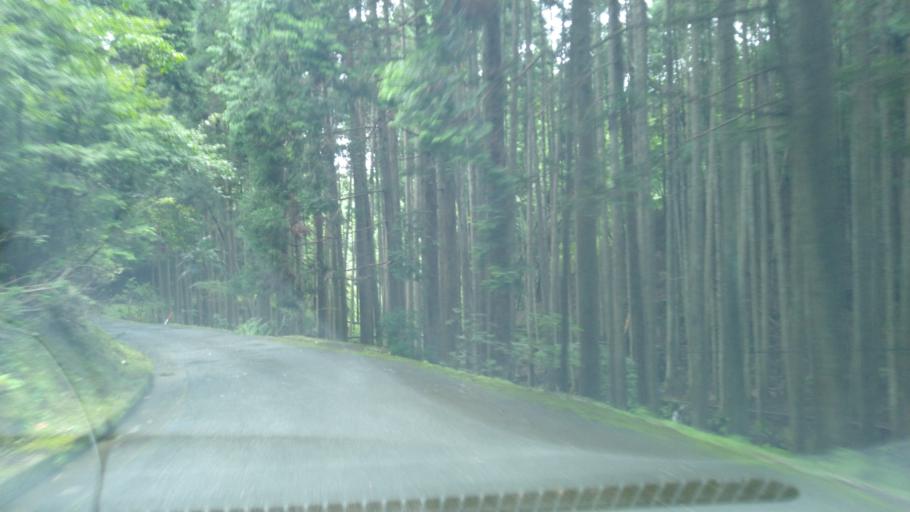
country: JP
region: Kyoto
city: Ayabe
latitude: 35.2342
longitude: 135.2674
